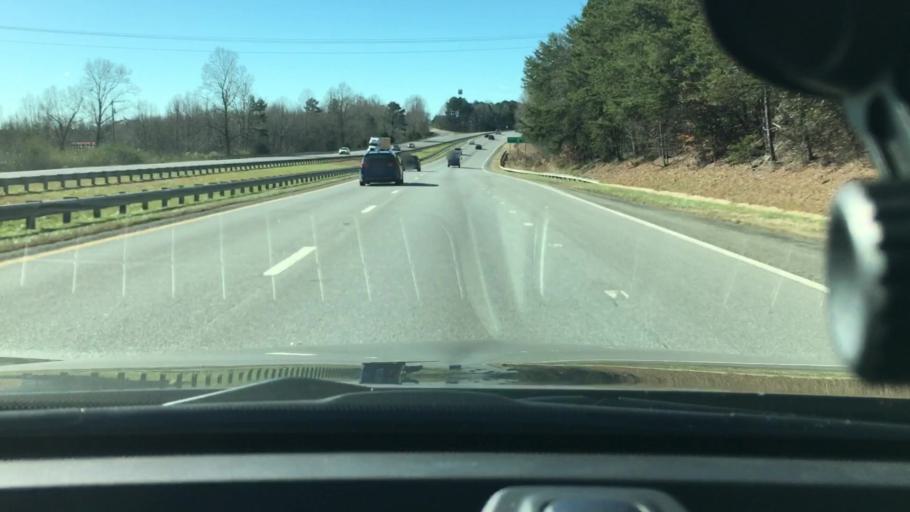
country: US
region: North Carolina
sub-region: Cleveland County
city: White Plains
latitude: 35.2042
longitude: -81.3628
